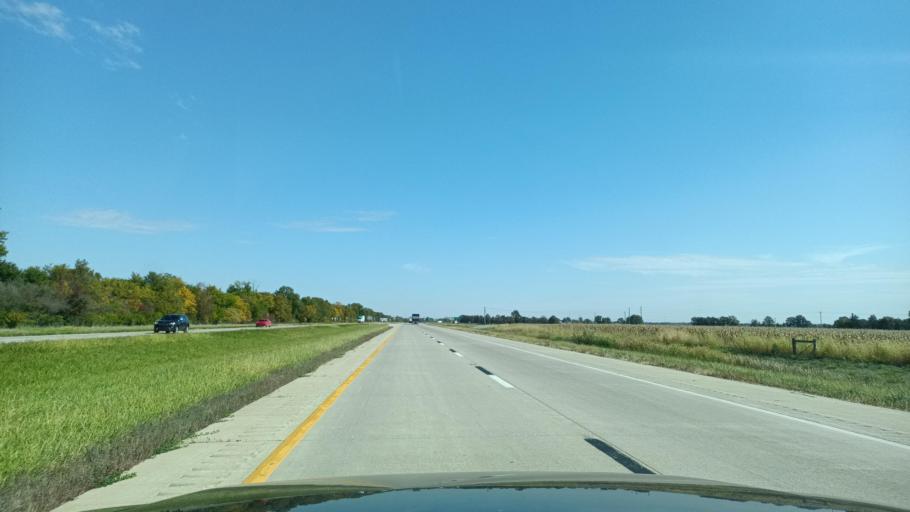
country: US
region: Ohio
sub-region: Paulding County
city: Paulding
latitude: 41.2080
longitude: -84.6355
